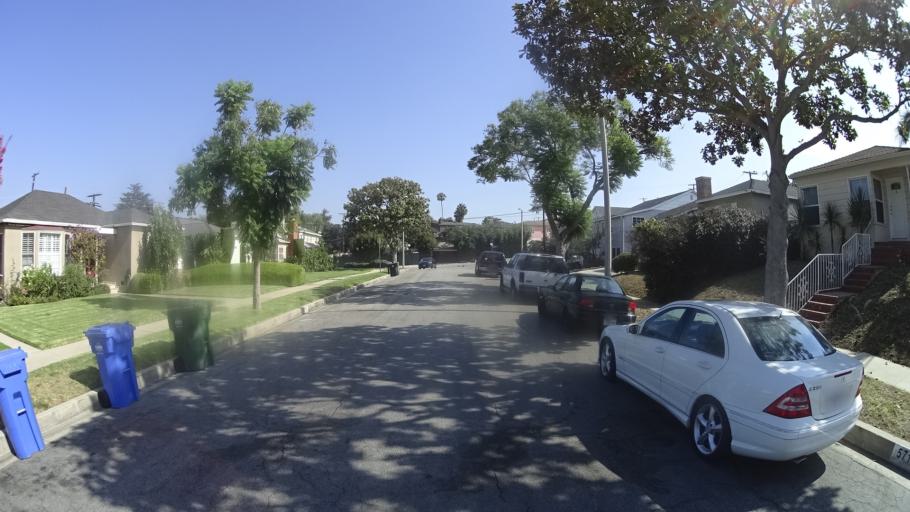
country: US
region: California
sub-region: Los Angeles County
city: View Park-Windsor Hills
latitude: 33.9900
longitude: -118.3448
